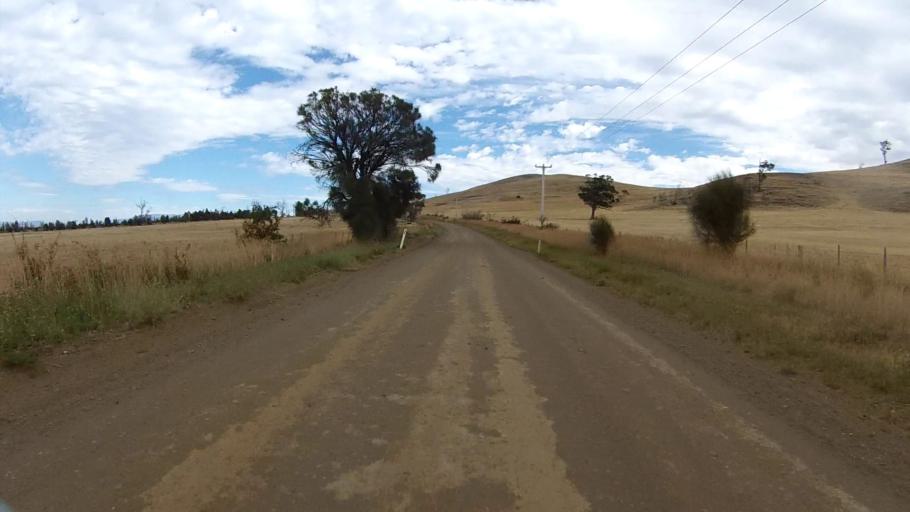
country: AU
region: Tasmania
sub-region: Sorell
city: Sorell
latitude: -42.8967
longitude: 147.7533
